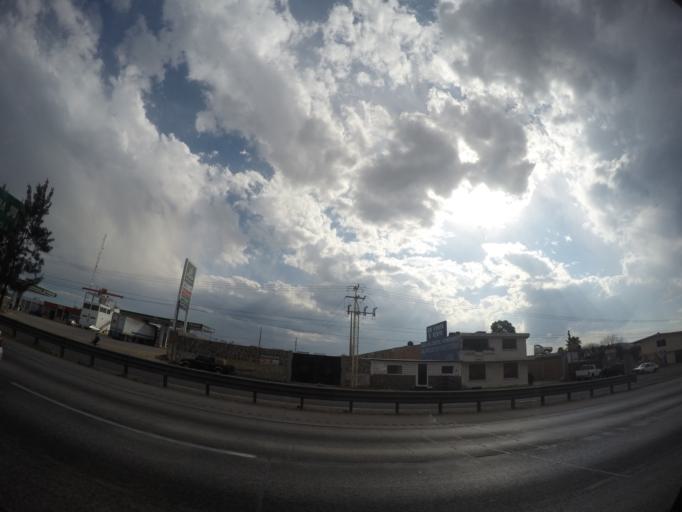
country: MX
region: Mexico
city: San Francisco Soyaniquilpan
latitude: 19.9887
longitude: -99.4554
